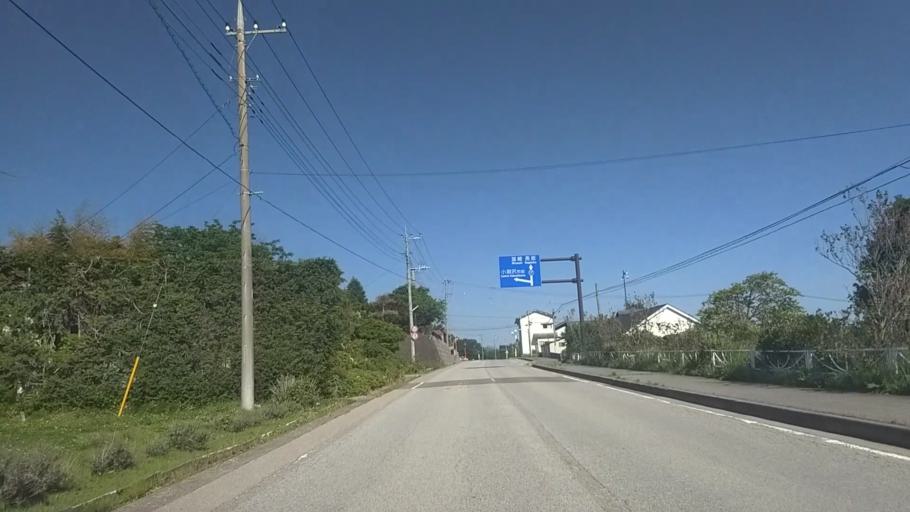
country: JP
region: Nagano
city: Chino
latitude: 35.8617
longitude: 138.3004
